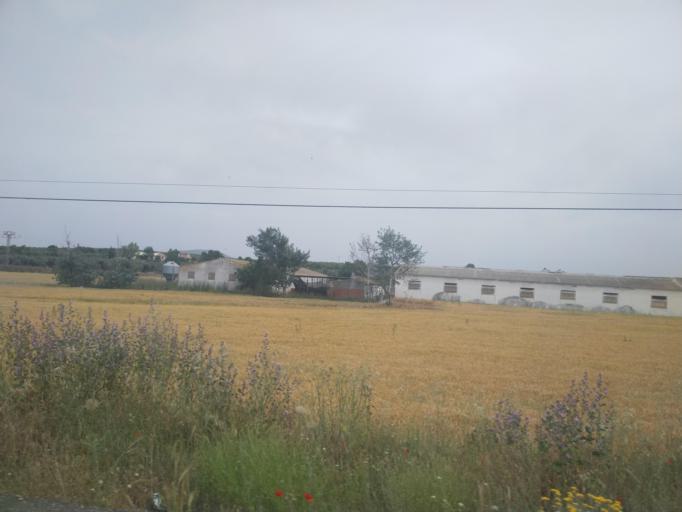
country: ES
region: Castille-La Mancha
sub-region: Province of Toledo
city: Guadamur
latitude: 39.7991
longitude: -4.1437
